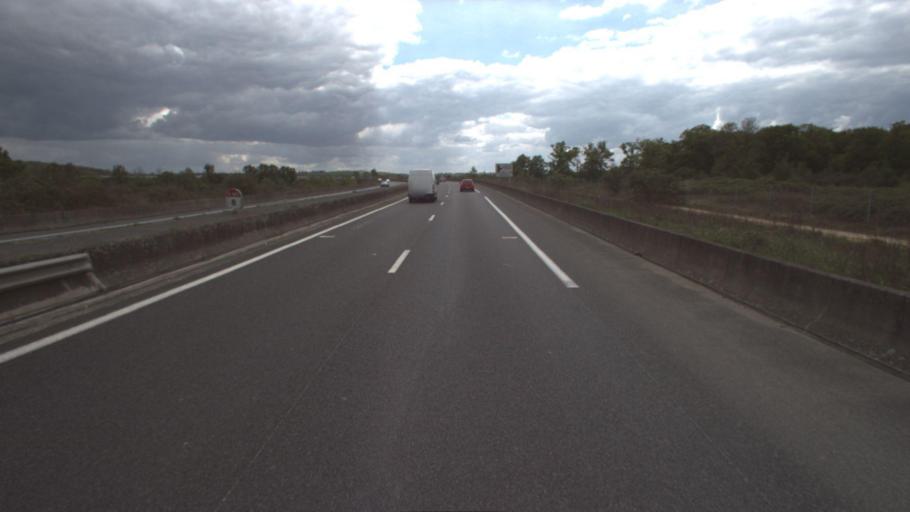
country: FR
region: Ile-de-France
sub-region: Departement de Seine-et-Marne
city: Mareuil-les-Meaux
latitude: 48.9266
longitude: 2.8450
